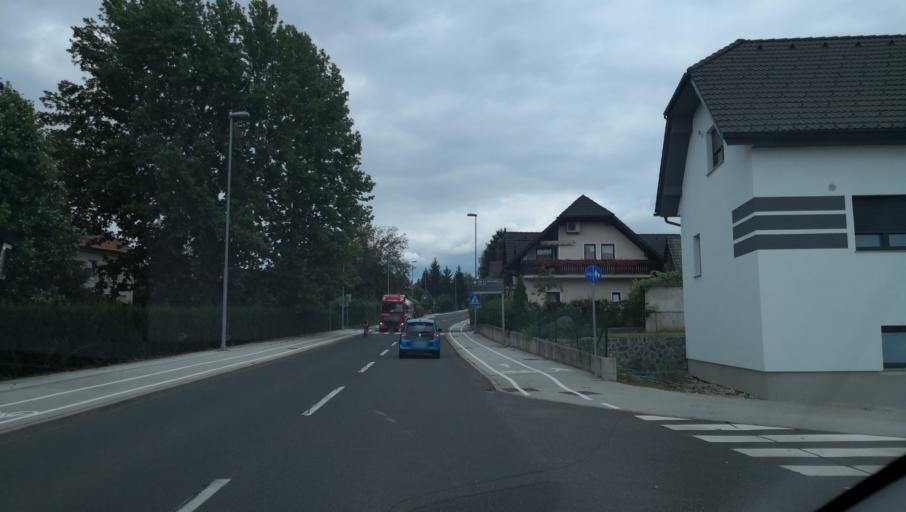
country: SI
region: Novo Mesto
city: Novo Mesto
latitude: 45.7889
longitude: 15.1793
